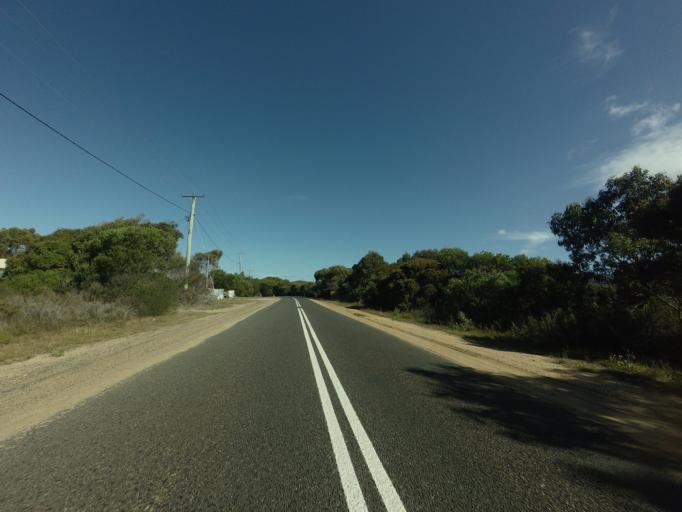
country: AU
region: Tasmania
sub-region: Break O'Day
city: St Helens
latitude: -41.8191
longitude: 148.2627
